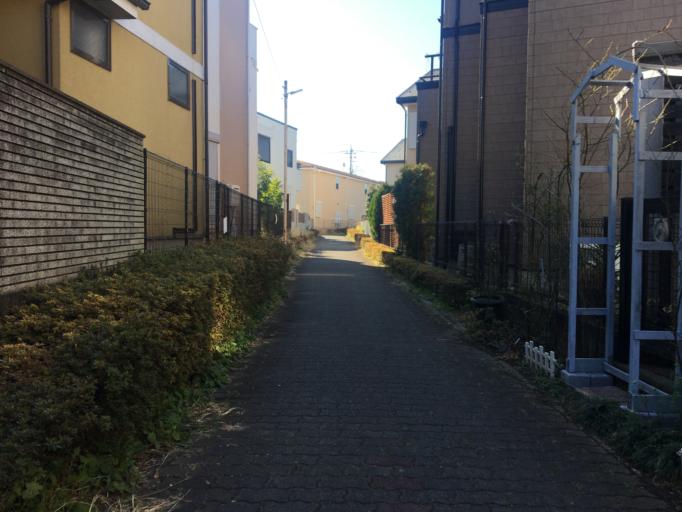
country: JP
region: Saitama
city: Shiki
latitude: 35.8134
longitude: 139.5733
